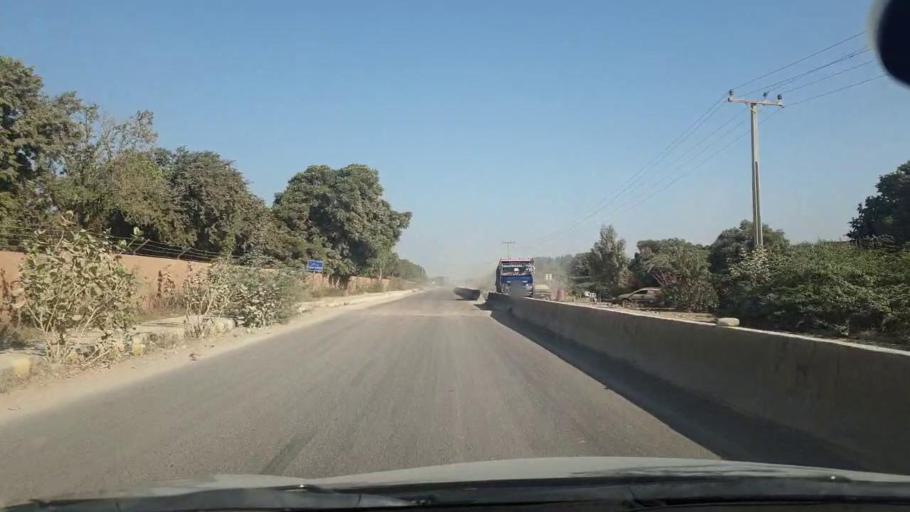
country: PK
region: Sindh
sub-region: Karachi District
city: Karachi
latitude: 25.0879
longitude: 67.0126
